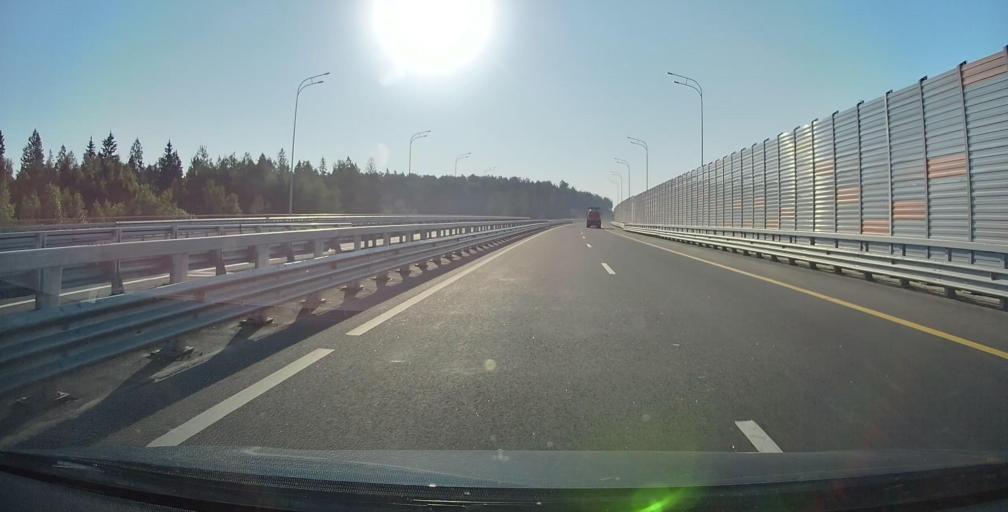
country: RU
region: Moskovskaya
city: Yel'digino
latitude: 56.1573
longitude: 37.7256
